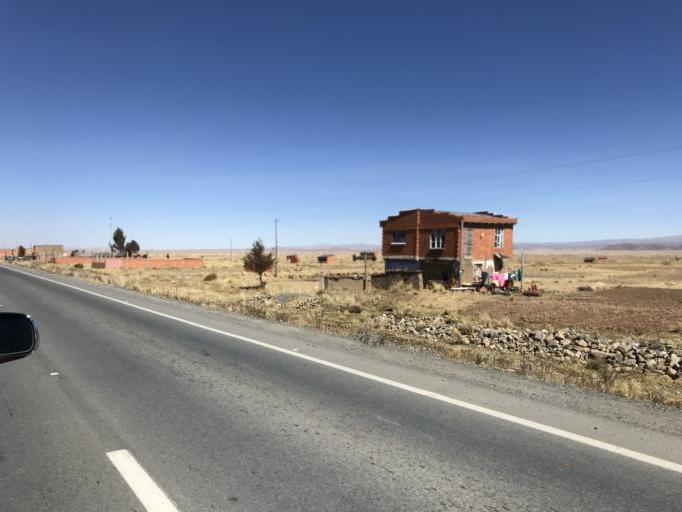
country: BO
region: La Paz
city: Batallas
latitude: -16.3738
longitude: -68.3828
